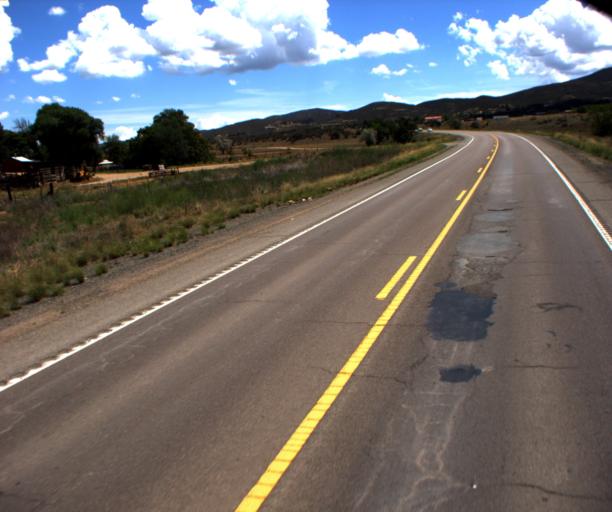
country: US
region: Arizona
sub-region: Yavapai County
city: Dewey-Humboldt
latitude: 34.5293
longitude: -112.2288
